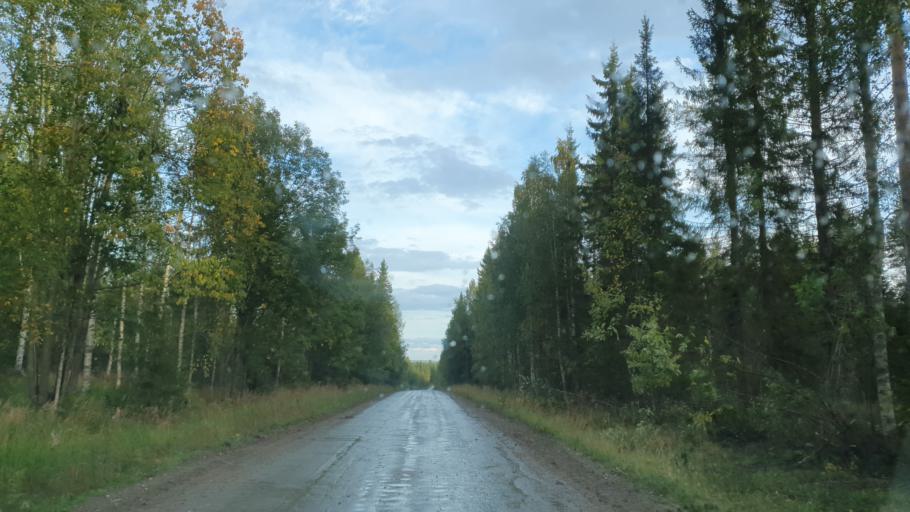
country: FI
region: Kainuu
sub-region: Kehys-Kainuu
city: Kuhmo
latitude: 64.3863
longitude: 29.4305
